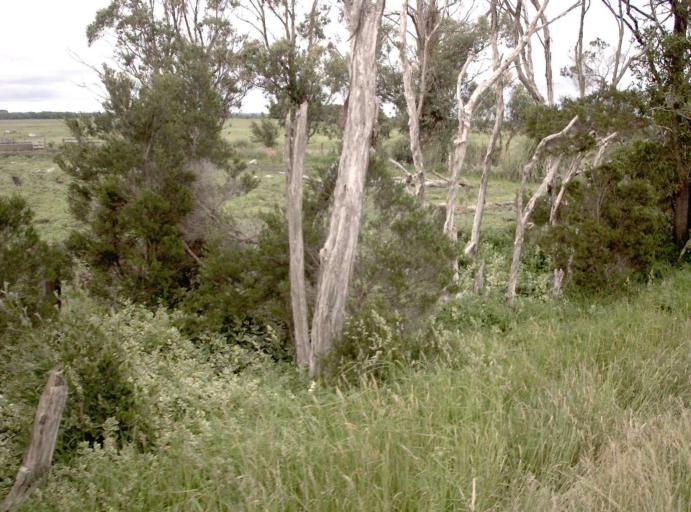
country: AU
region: Victoria
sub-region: Bass Coast
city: North Wonthaggi
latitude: -38.5511
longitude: 145.6825
